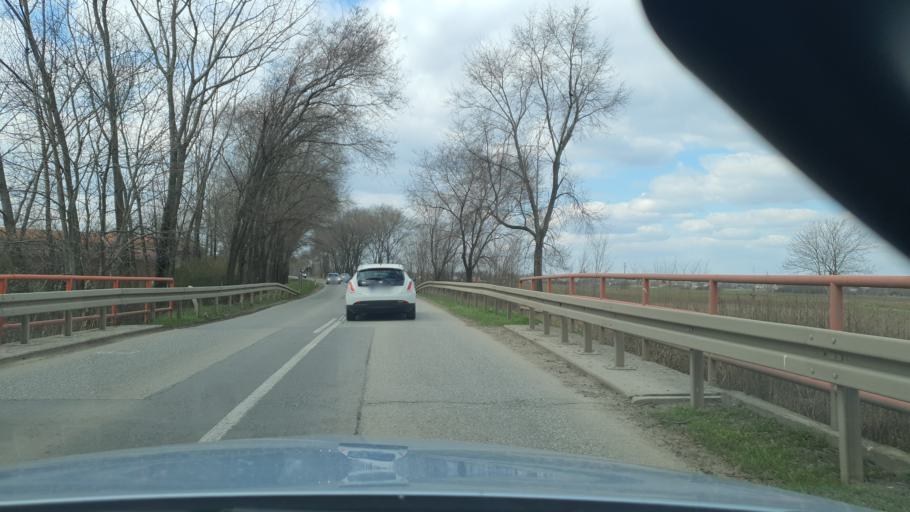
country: RS
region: Autonomna Pokrajina Vojvodina
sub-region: Zapadnobacki Okrug
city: Odzaci
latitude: 45.4488
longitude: 19.3545
